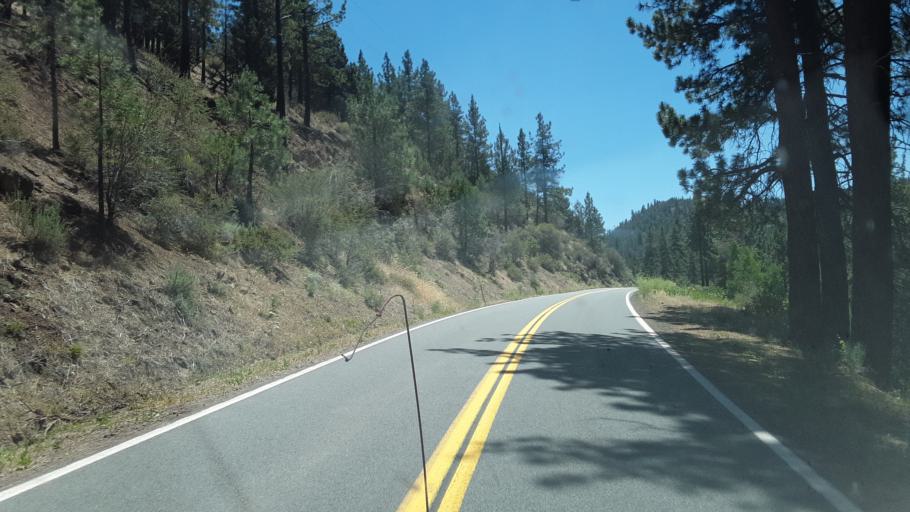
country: US
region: California
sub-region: Modoc County
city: Alturas
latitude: 41.0325
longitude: -120.8541
